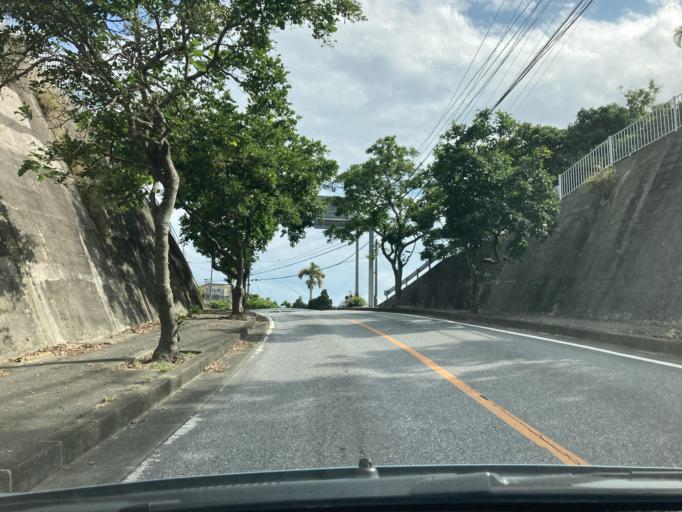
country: JP
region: Okinawa
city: Ginowan
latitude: 26.2712
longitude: 127.7811
